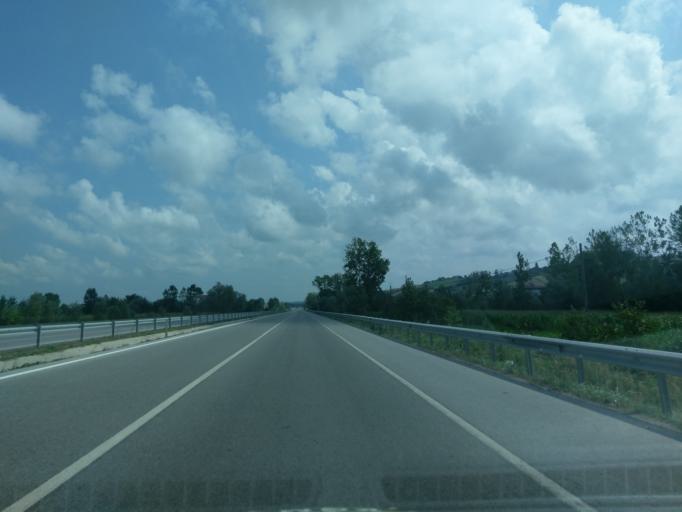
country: TR
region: Samsun
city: Alacam
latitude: 41.6110
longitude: 35.7167
